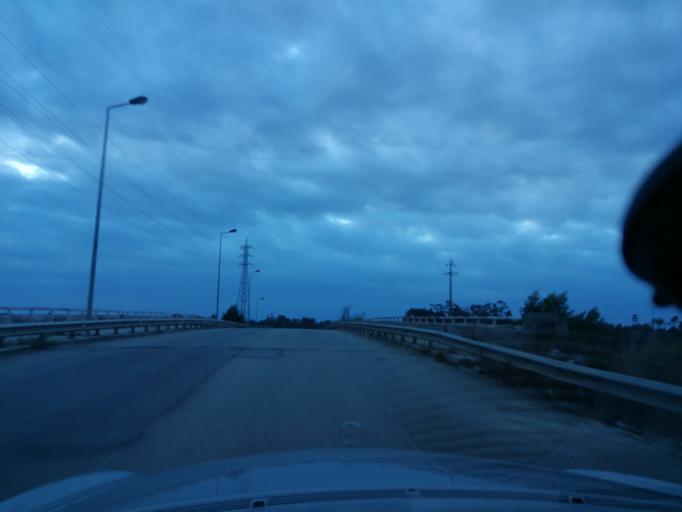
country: PT
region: Aveiro
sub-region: Estarreja
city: Estarreja
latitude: 40.7687
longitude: -8.5771
